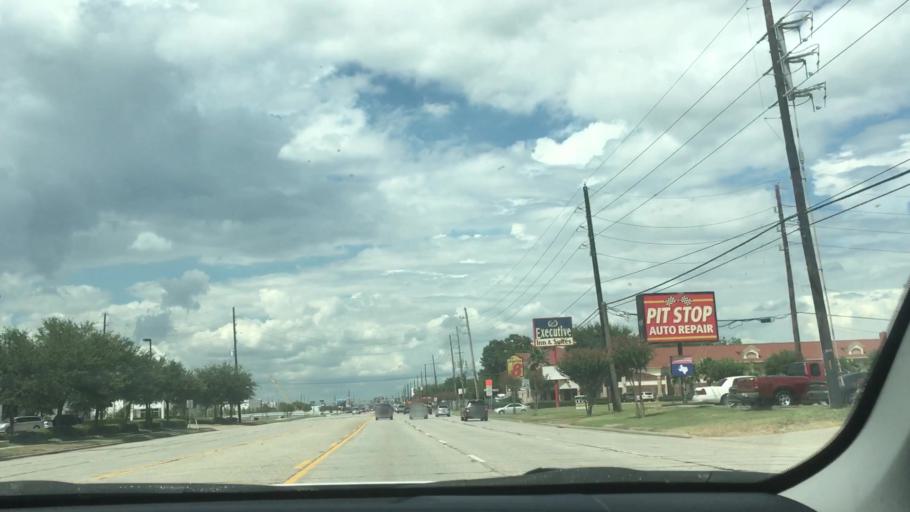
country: US
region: Texas
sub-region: Fort Bend County
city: Stafford
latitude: 29.6354
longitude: -95.5650
